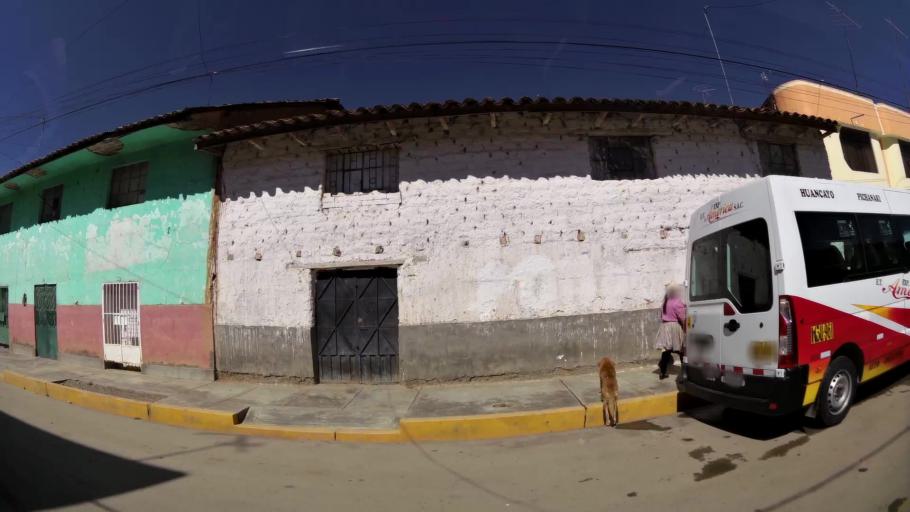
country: PE
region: Junin
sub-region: Provincia de Huancayo
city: San Jeronimo
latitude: -11.9426
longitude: -75.2929
